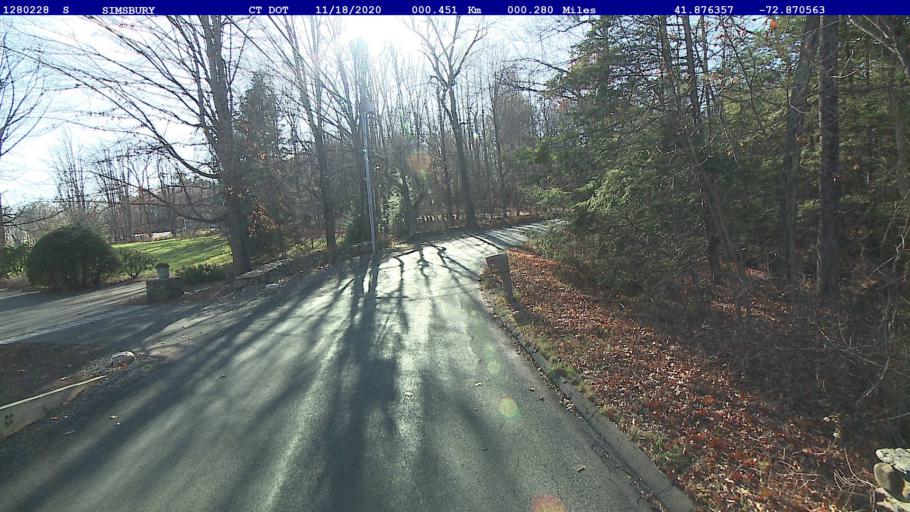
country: US
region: Connecticut
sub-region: Hartford County
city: West Simsbury
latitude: 41.8764
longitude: -72.8706
